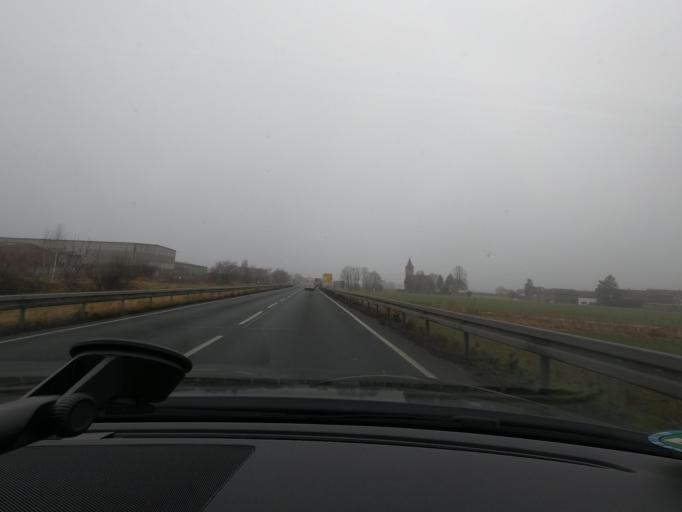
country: DE
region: North Rhine-Westphalia
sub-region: Regierungsbezirk Koln
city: Merzenich
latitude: 50.8102
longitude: 6.5167
